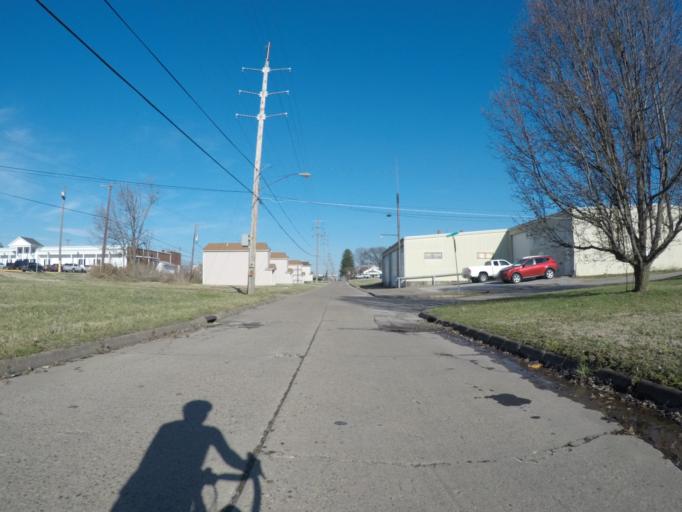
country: US
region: West Virginia
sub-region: Cabell County
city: Huntington
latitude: 38.4085
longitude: -82.4888
